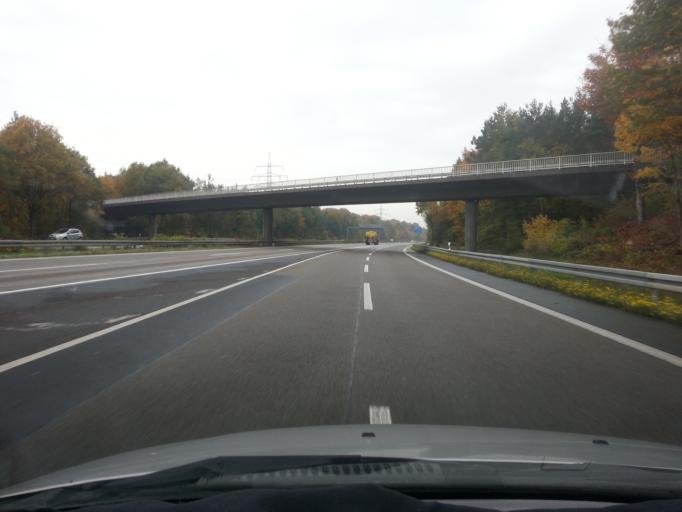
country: DE
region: Hesse
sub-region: Regierungsbezirk Darmstadt
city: Neu Isenburg
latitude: 50.0358
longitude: 8.7134
